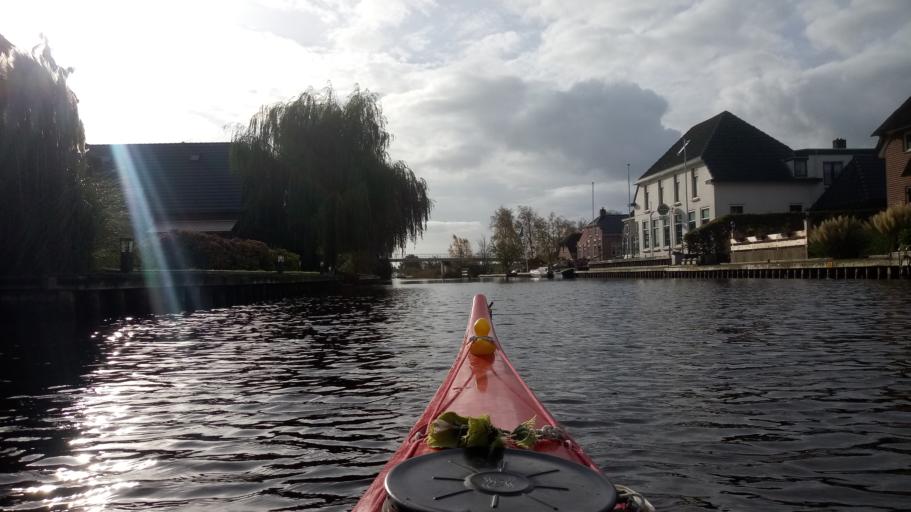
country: NL
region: Overijssel
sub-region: Gemeente Steenwijkerland
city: Sint Jansklooster
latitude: 52.6684
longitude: 6.0529
